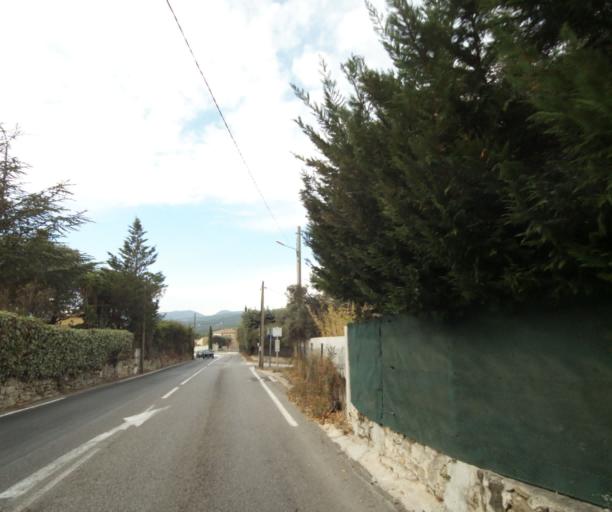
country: FR
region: Provence-Alpes-Cote d'Azur
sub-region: Departement des Bouches-du-Rhone
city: Ceyreste
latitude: 43.2207
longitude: 5.6434
